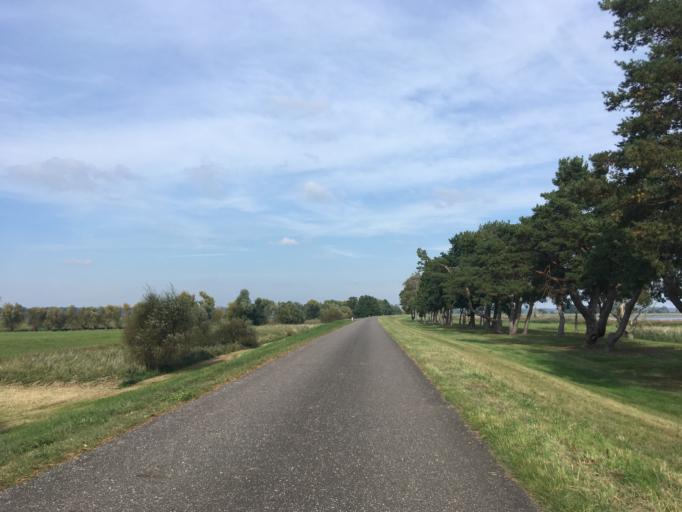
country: DE
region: Brandenburg
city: Schoneberg
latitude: 52.9551
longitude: 14.1373
